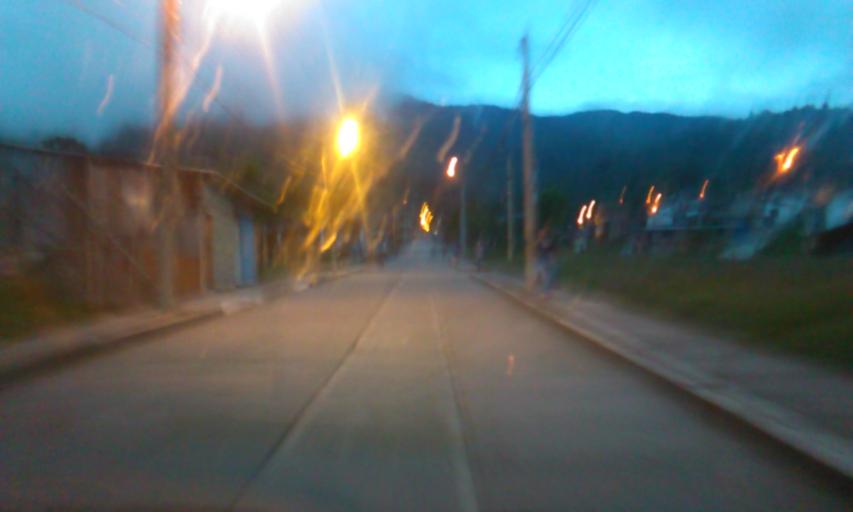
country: CO
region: Quindio
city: Cordoba
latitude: 4.3927
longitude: -75.6886
